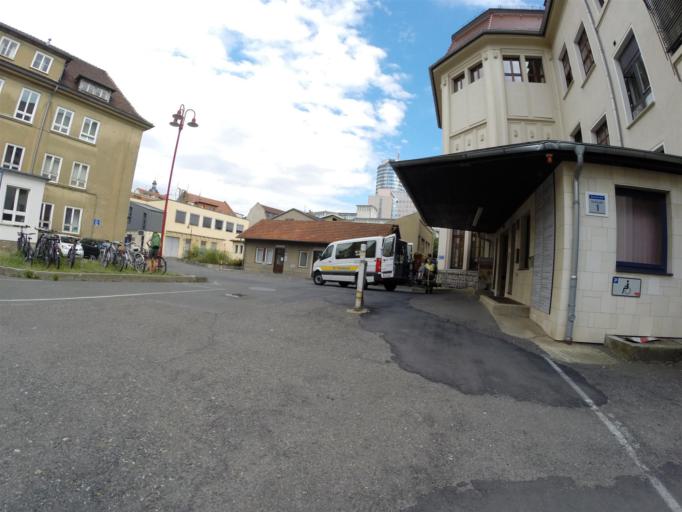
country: DE
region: Thuringia
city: Jena
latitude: 50.9291
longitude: 11.5797
